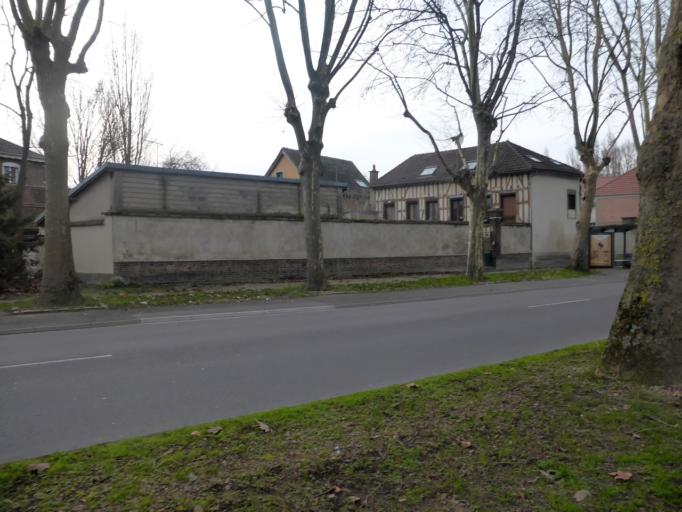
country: FR
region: Champagne-Ardenne
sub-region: Departement de l'Aube
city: Troyes
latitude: 48.3006
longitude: 4.0869
